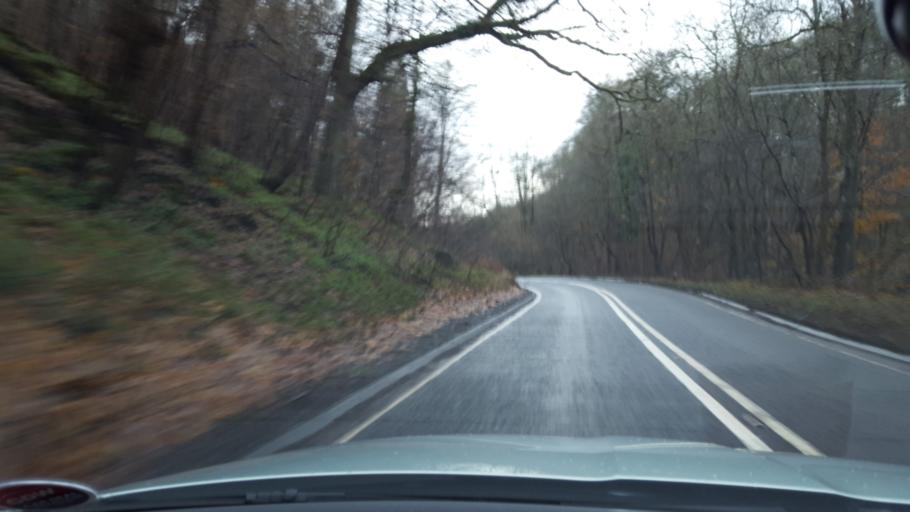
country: GB
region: Scotland
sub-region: Perth and Kinross
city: Abernethy
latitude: 56.3124
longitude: -3.3560
